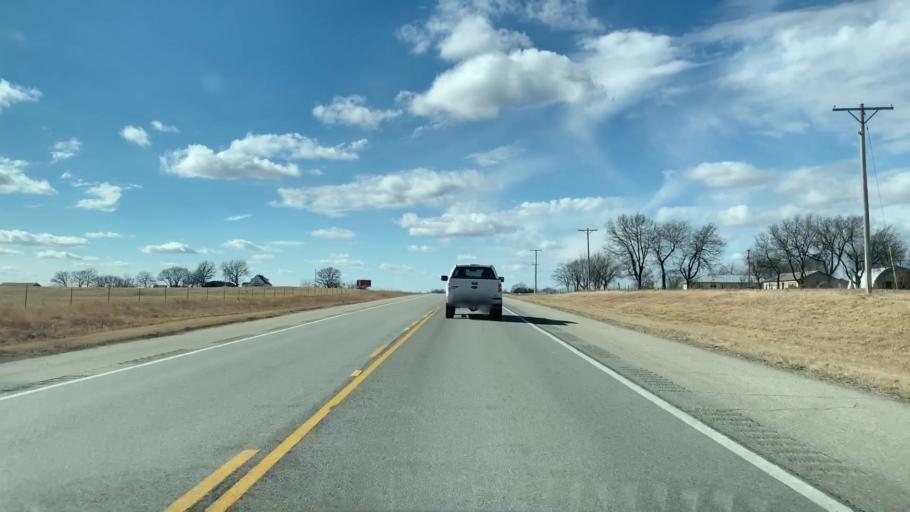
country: US
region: Kansas
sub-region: Labette County
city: Parsons
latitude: 37.3400
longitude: -95.1714
